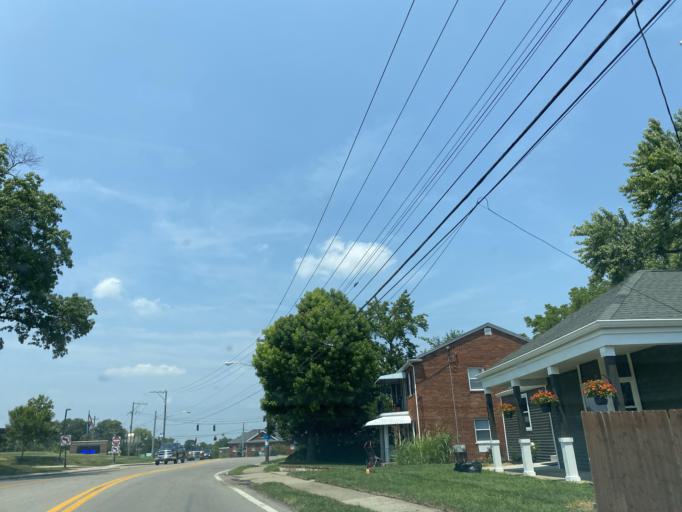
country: US
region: Kentucky
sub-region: Campbell County
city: Fort Thomas
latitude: 39.0585
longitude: -84.4508
